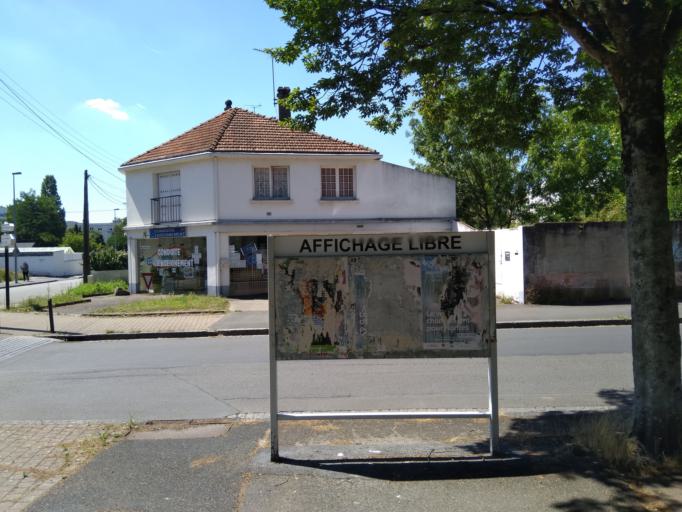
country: FR
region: Pays de la Loire
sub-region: Departement de la Loire-Atlantique
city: Bouguenais
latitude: 47.2090
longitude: -1.6045
